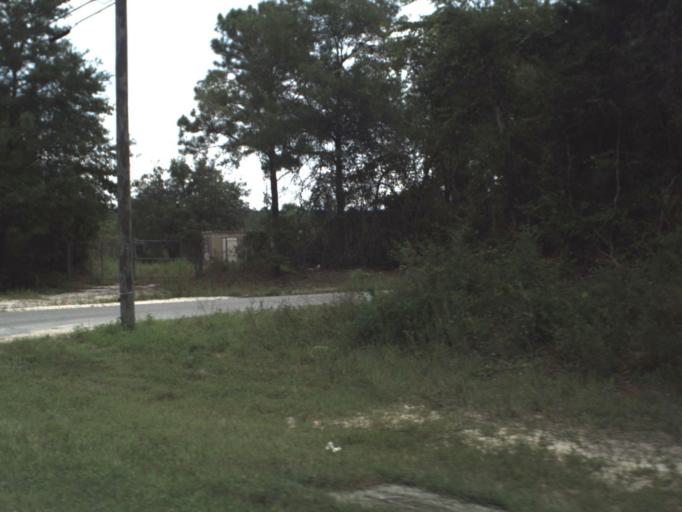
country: US
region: Florida
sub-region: Bay County
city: Hiland Park
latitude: 30.2332
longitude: -85.5909
